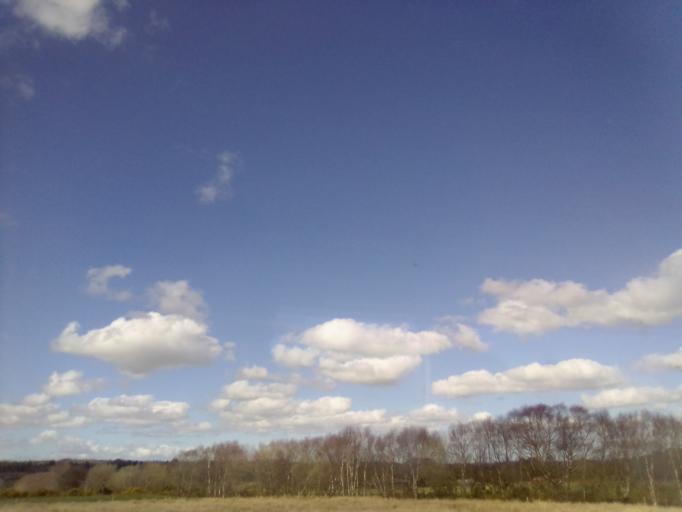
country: IE
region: Munster
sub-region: County Cork
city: Millstreet
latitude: 52.0773
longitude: -9.1671
